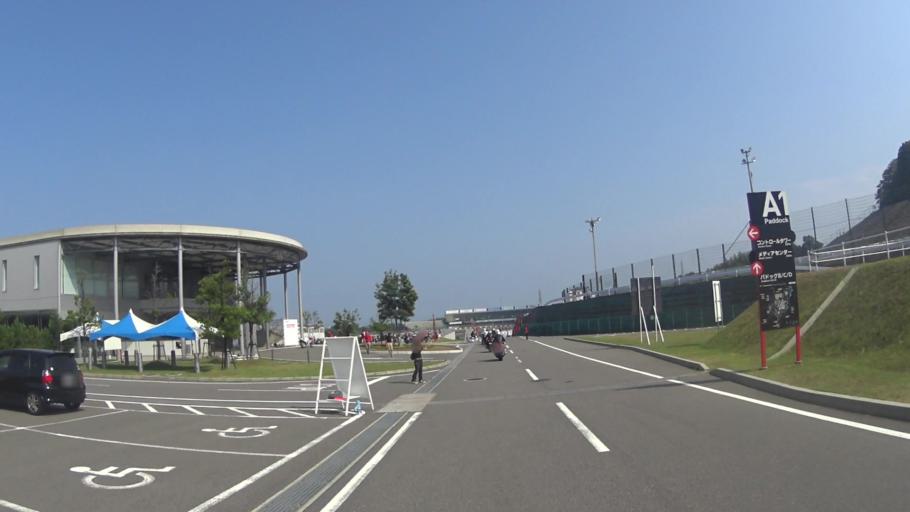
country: JP
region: Mie
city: Kawage
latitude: 34.8432
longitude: 136.5388
